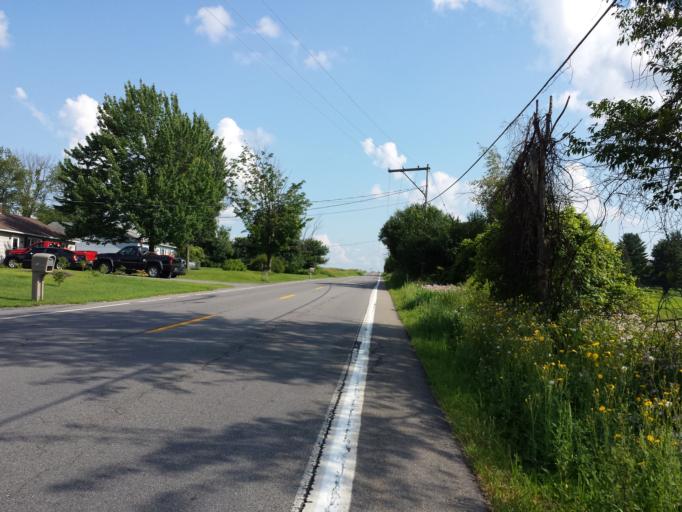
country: US
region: New York
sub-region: St. Lawrence County
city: Hannawa Falls
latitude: 44.6337
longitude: -74.9572
